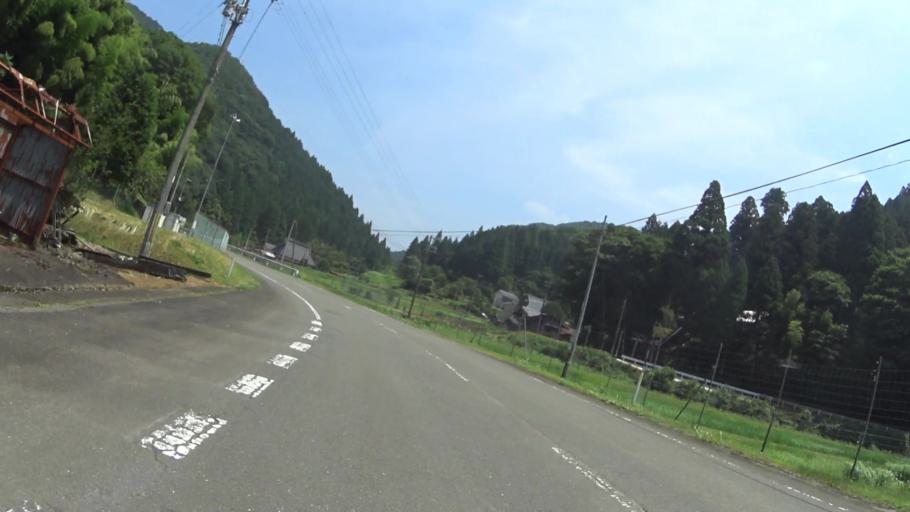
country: JP
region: Kyoto
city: Maizuru
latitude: 35.3072
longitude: 135.4308
